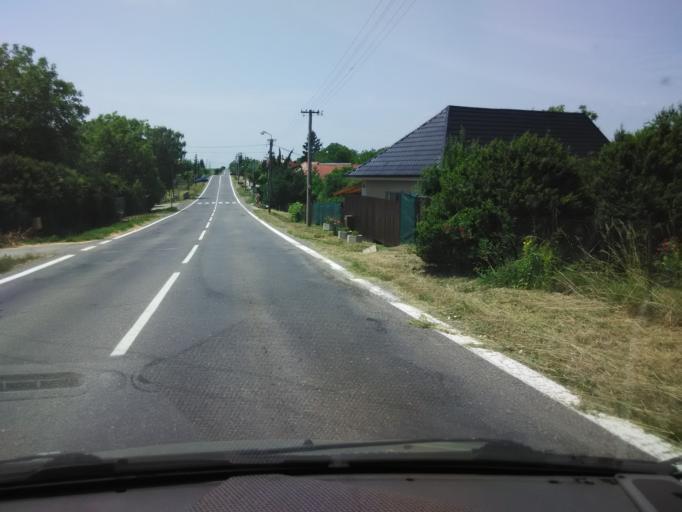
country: SK
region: Nitriansky
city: Levice
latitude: 48.2365
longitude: 18.6611
